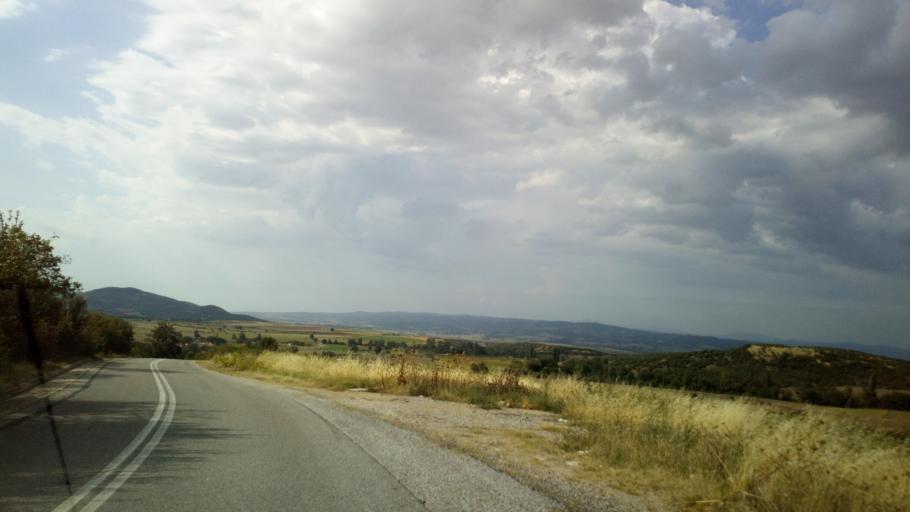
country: GR
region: Central Macedonia
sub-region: Nomos Chalkidikis
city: Galatista
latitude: 40.5024
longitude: 23.3841
